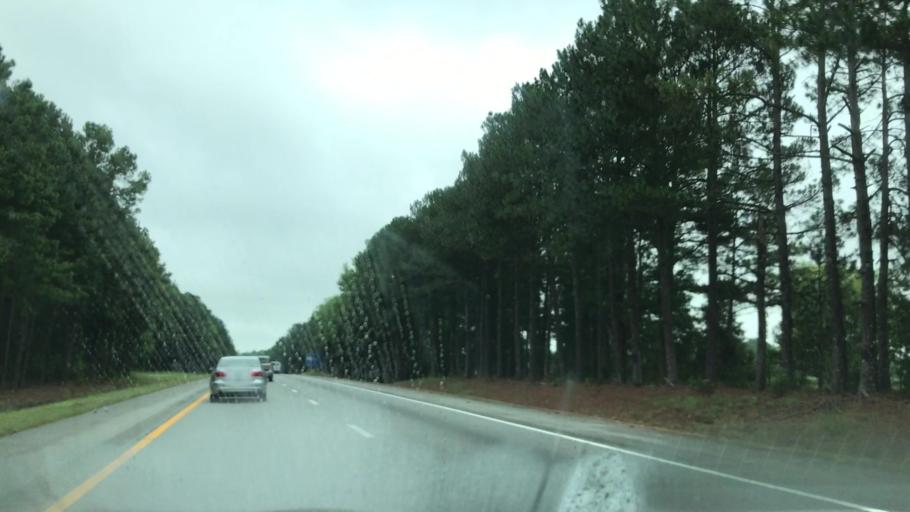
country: US
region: North Carolina
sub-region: Halifax County
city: Weldon
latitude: 36.3788
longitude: -77.6598
